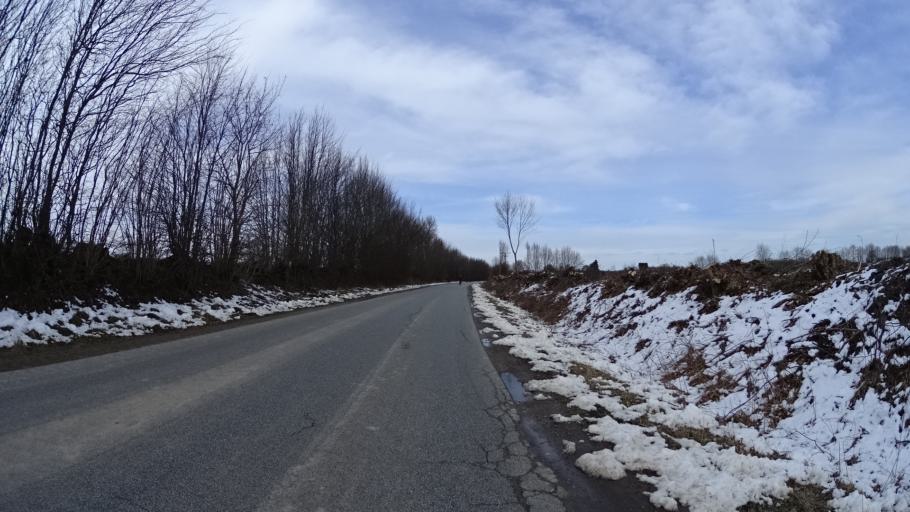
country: DE
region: Schleswig-Holstein
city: Loptin
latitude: 54.1794
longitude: 10.2193
